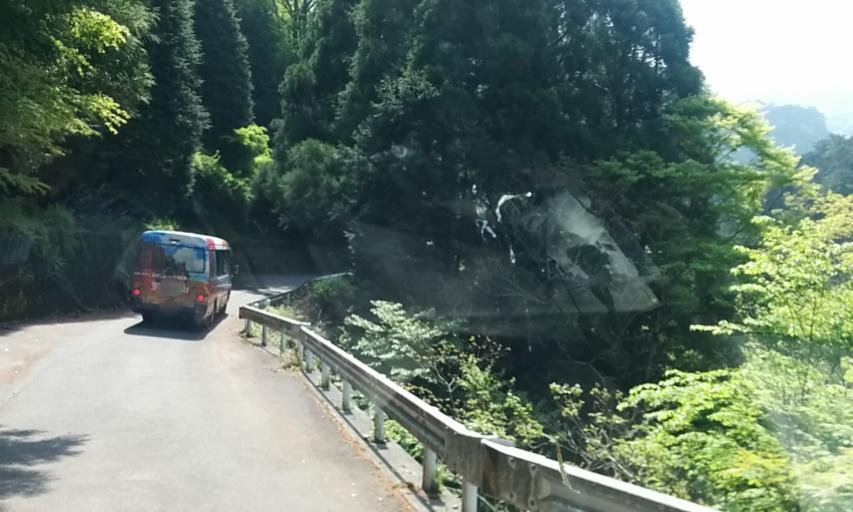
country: JP
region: Ehime
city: Niihama
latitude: 33.8689
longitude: 133.2945
